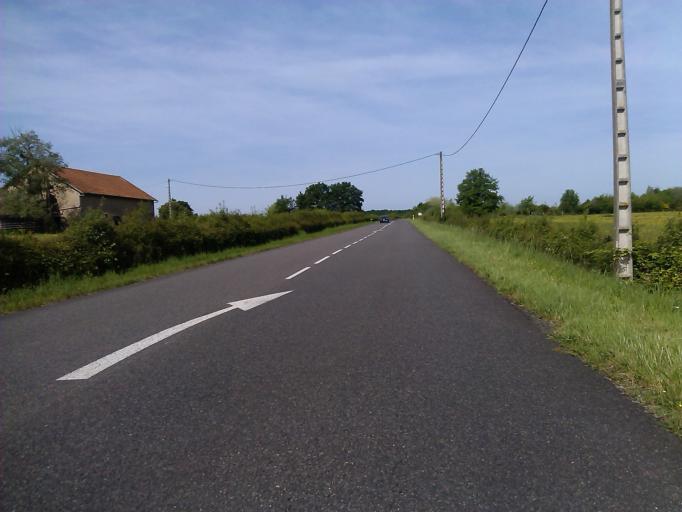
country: FR
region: Auvergne
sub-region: Departement de l'Allier
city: Dompierre-sur-Besbre
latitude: 46.5332
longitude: 3.6455
